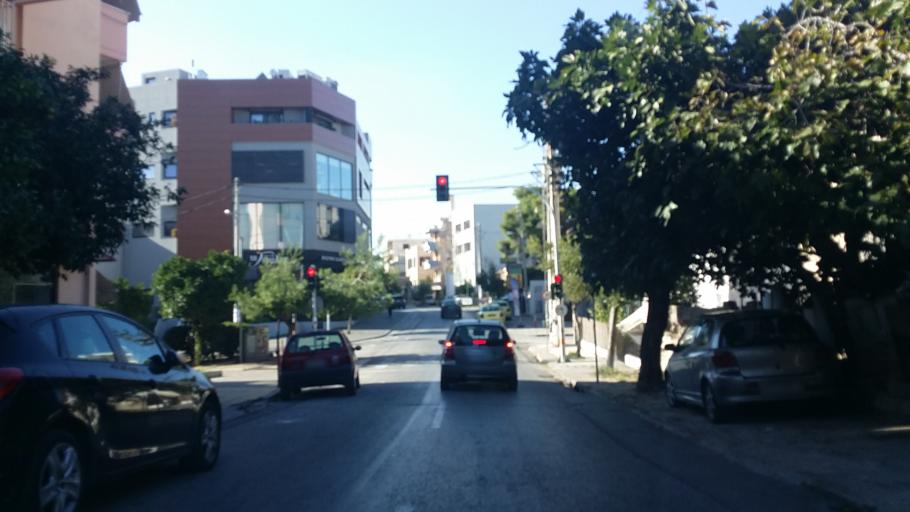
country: GR
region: Attica
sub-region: Nomarchia Athinas
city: Nea Ionia
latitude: 38.0415
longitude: 23.7641
